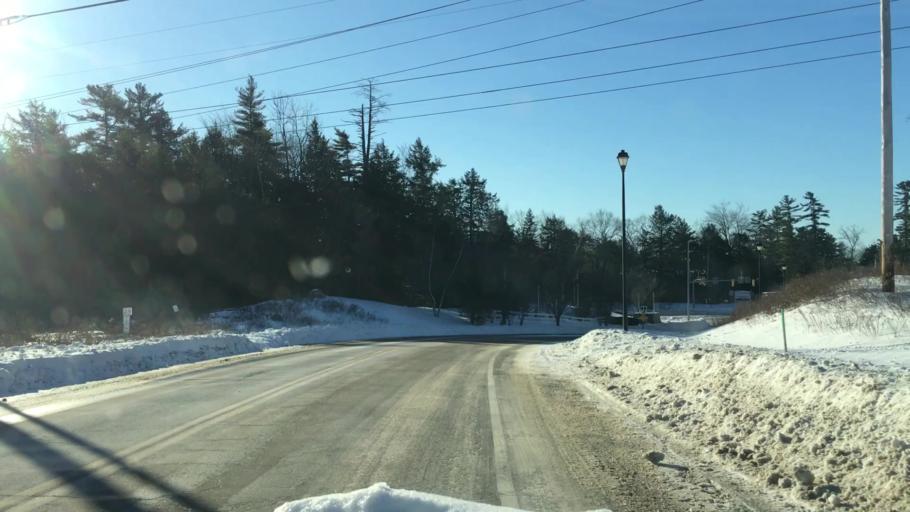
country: US
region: Maine
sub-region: Sagadahoc County
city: Topsham
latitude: 43.9373
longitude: -69.9562
